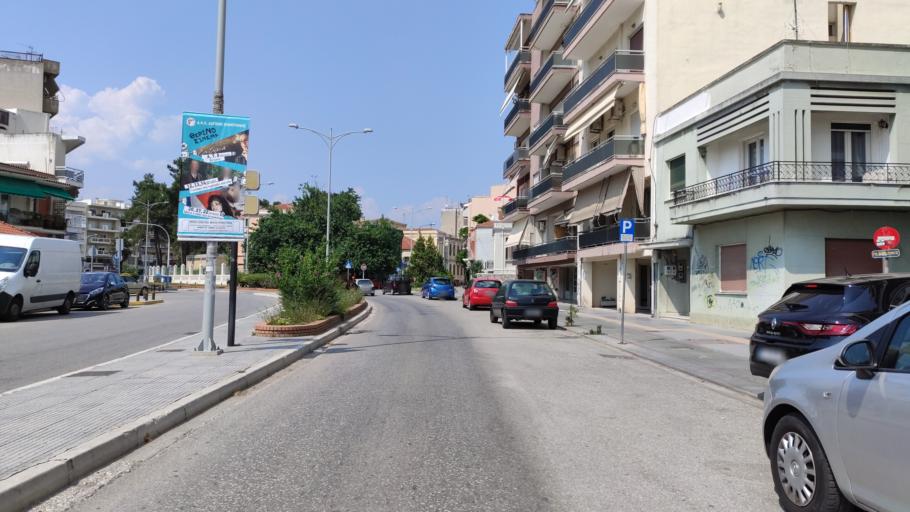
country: GR
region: East Macedonia and Thrace
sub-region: Nomos Rodopis
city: Komotini
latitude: 41.1178
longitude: 25.3980
